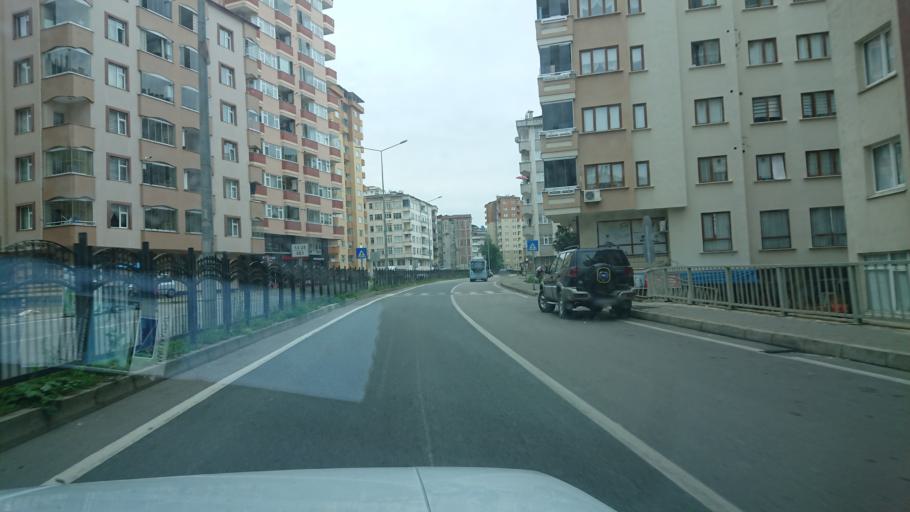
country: TR
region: Rize
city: Rize
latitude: 41.0231
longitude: 40.5385
